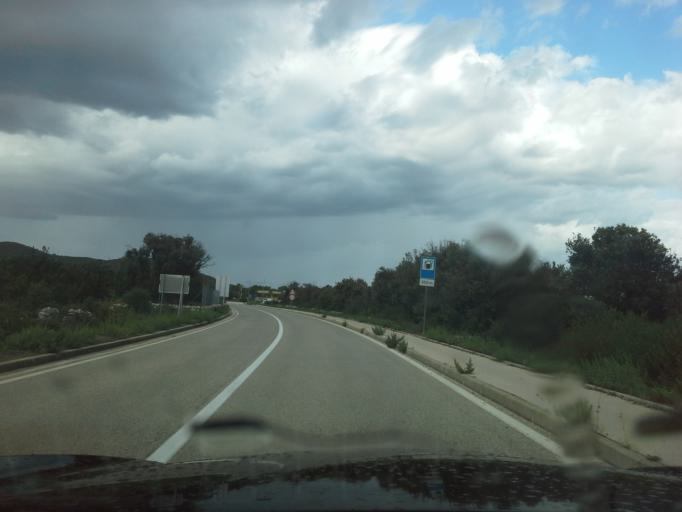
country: HR
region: Primorsko-Goranska
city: Mali Losinj
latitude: 44.6697
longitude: 14.3972
